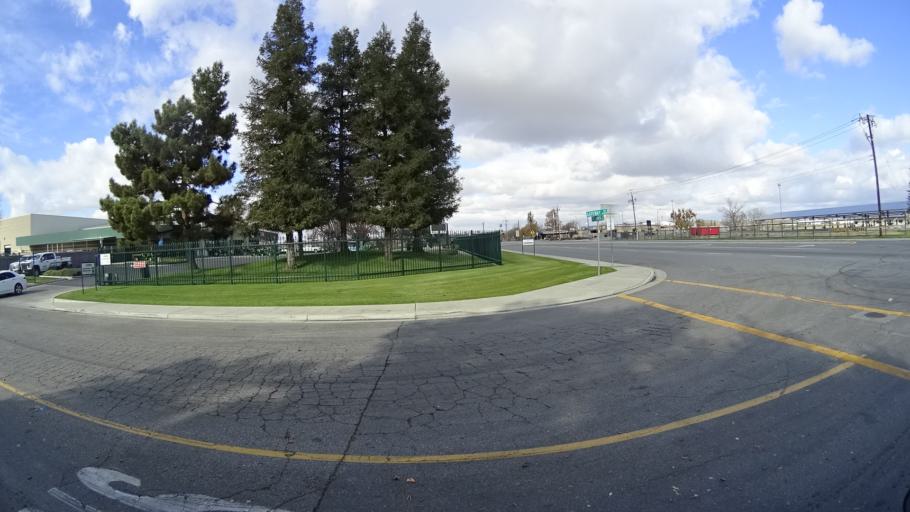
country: US
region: California
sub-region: Kern County
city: Bakersfield
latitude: 35.3498
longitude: -118.9678
